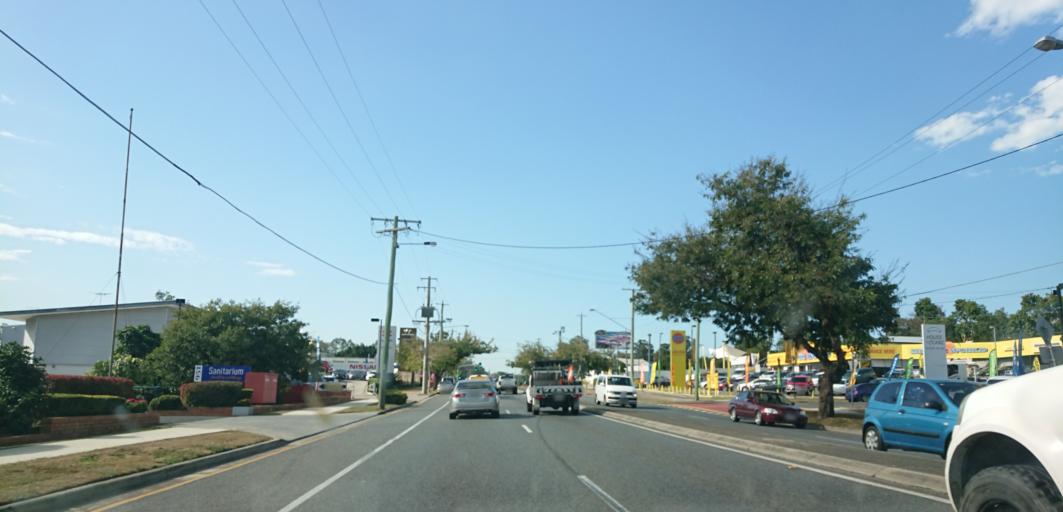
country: AU
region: Queensland
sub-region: Brisbane
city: Yeerongpilly
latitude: -27.5285
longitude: 153.0199
